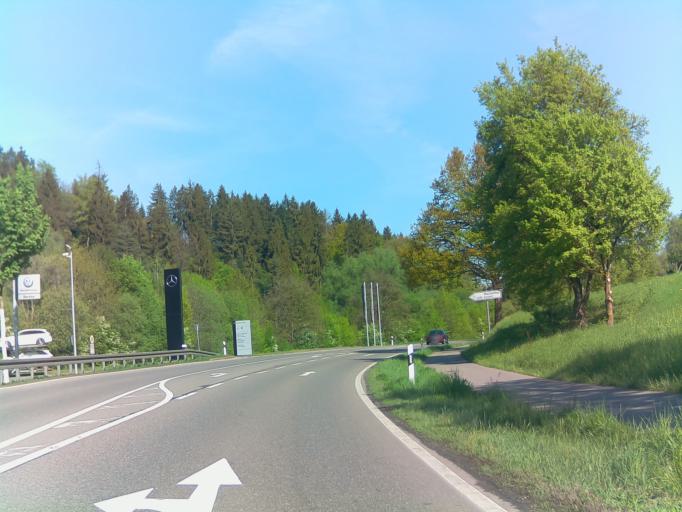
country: DE
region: Baden-Wuerttemberg
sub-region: Karlsruhe Region
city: Rohrdorf
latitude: 48.5548
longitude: 8.7063
